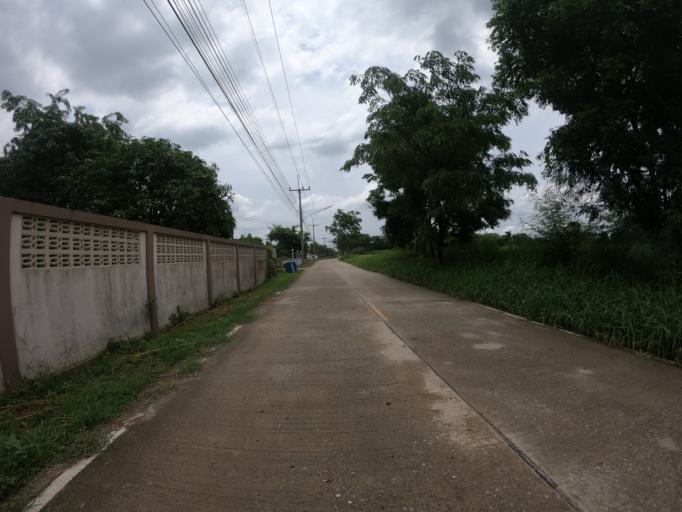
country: TH
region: Pathum Thani
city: Ban Lam Luk Ka
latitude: 13.9681
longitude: 100.8540
